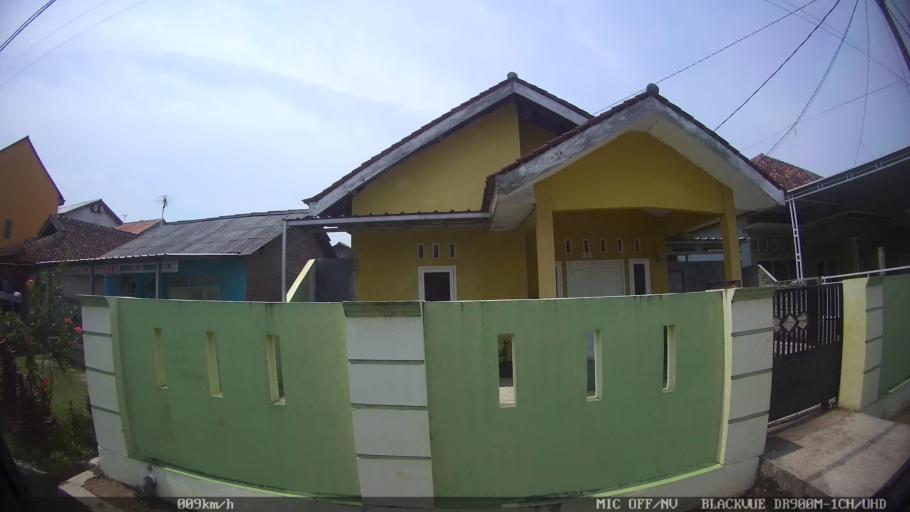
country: ID
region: Lampung
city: Bandarlampung
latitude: -5.4491
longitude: 105.2494
